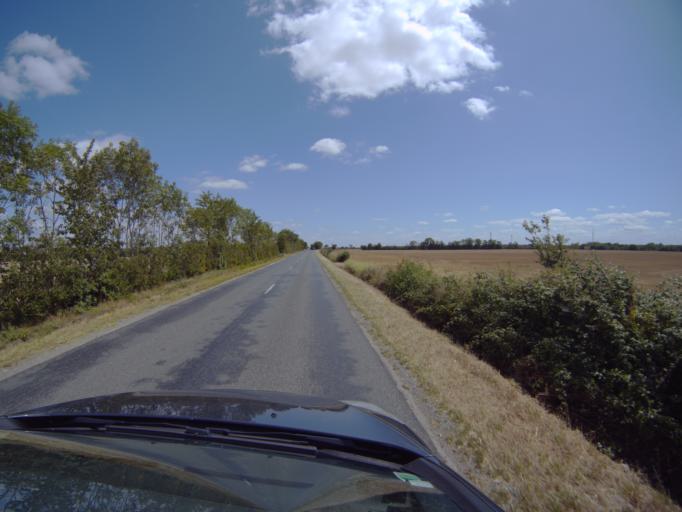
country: FR
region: Poitou-Charentes
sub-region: Departement de la Charente-Maritime
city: Saint-Jean-de-Liversay
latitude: 46.2585
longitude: -0.8533
